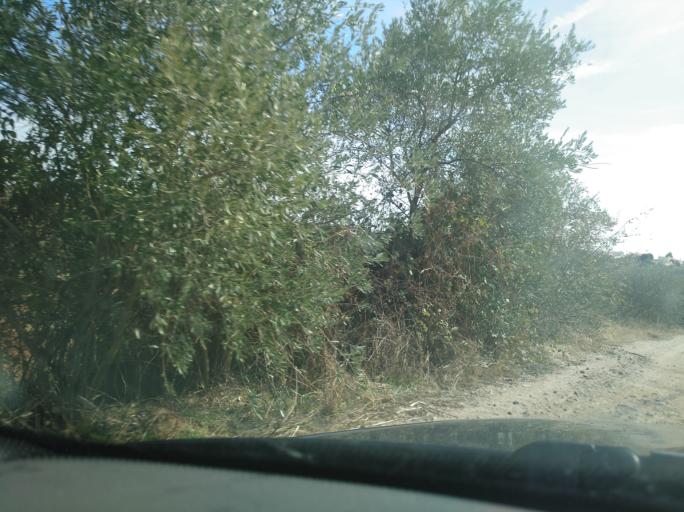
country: PT
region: Portalegre
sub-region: Campo Maior
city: Campo Maior
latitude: 39.0380
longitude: -7.0511
